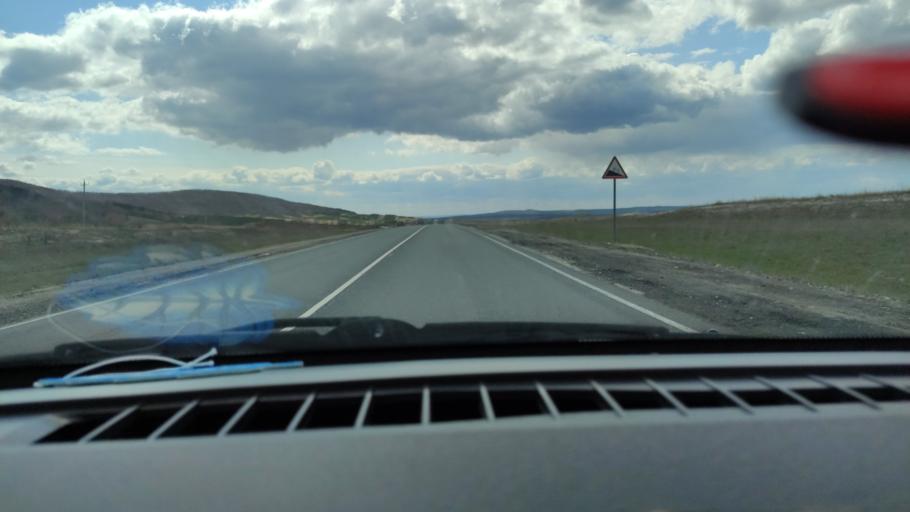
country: RU
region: Saratov
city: Alekseyevka
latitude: 52.3152
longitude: 47.9232
